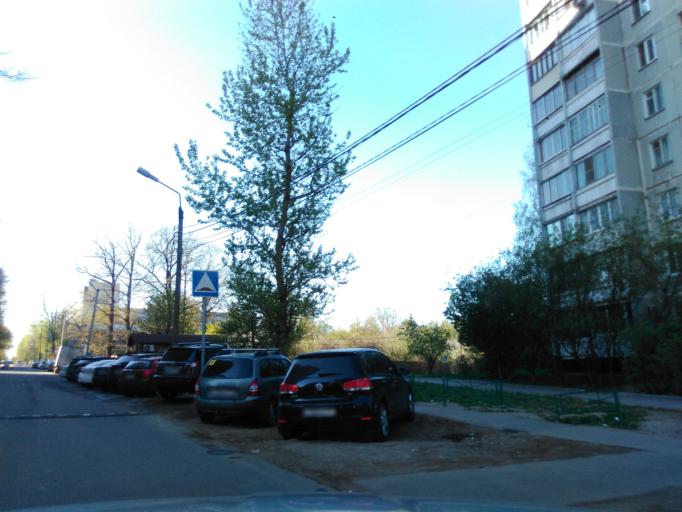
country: RU
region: Moskovskaya
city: Skhodnya
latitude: 55.9468
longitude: 37.3002
